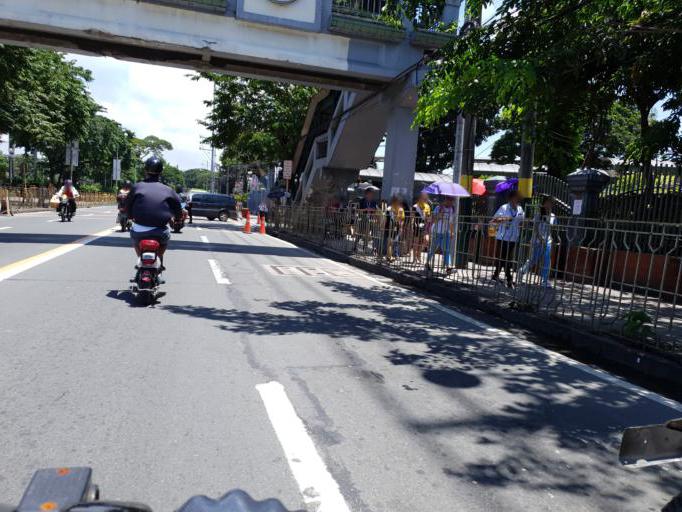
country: PH
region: Metro Manila
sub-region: Pasig
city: Pasig City
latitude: 14.5644
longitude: 121.0556
